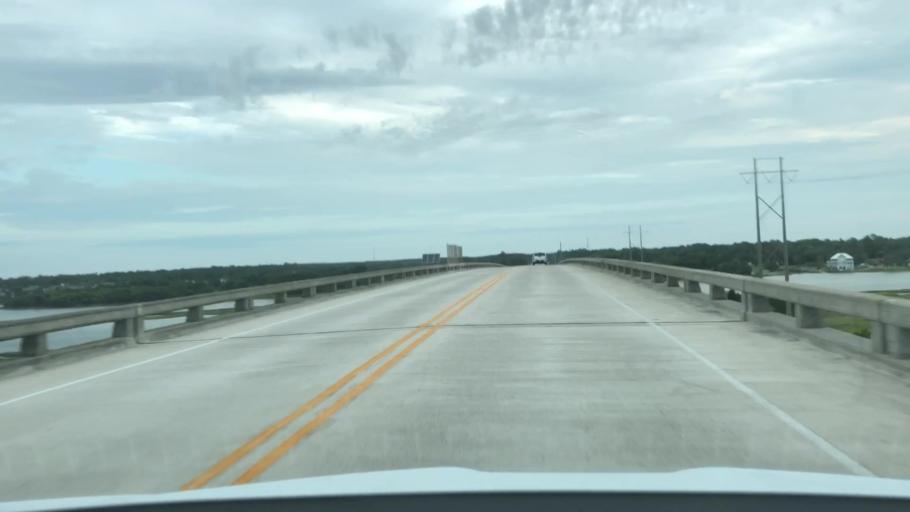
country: US
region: North Carolina
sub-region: Carteret County
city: Cedar Point
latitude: 34.6737
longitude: -77.0652
